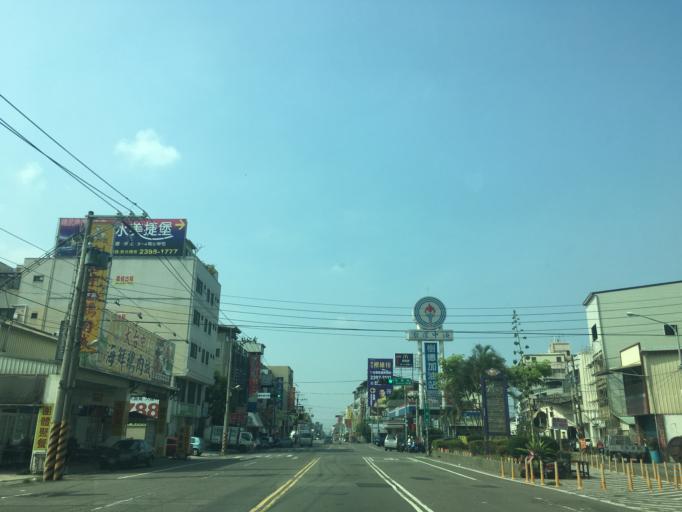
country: TW
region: Taiwan
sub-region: Taichung City
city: Taichung
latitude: 24.1588
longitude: 120.7129
